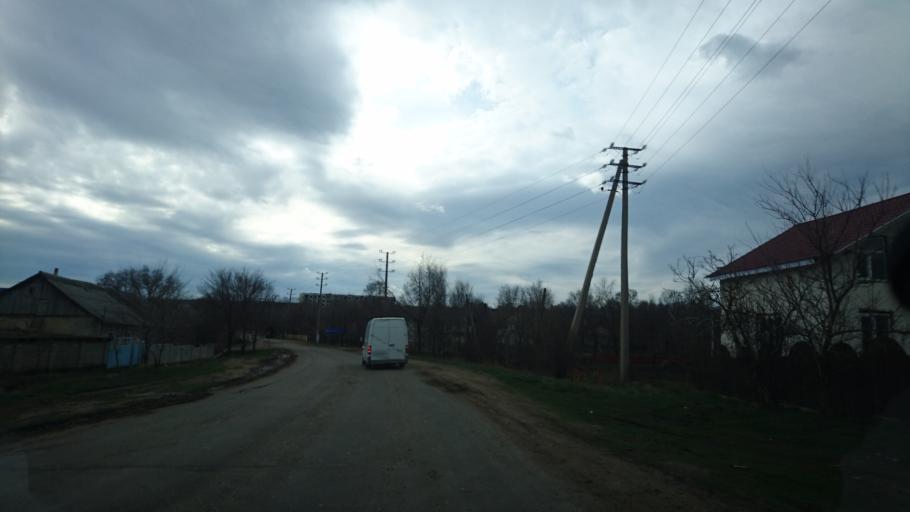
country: MD
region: Cantemir
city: Visniovca
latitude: 46.3334
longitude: 28.4523
